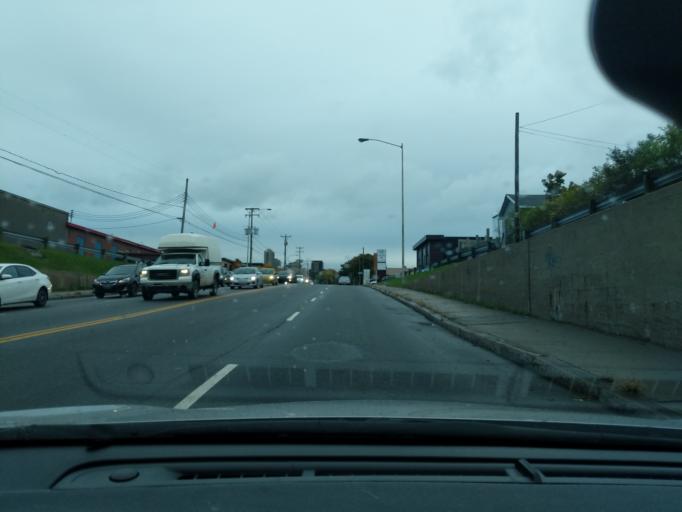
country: CA
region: Quebec
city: Quebec
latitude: 46.8033
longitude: -71.2633
